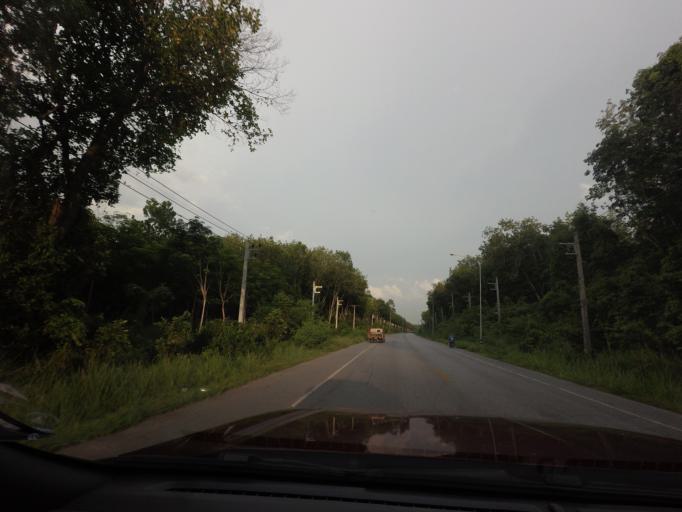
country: TH
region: Pattani
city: Khok Pho
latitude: 6.6728
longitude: 101.1557
